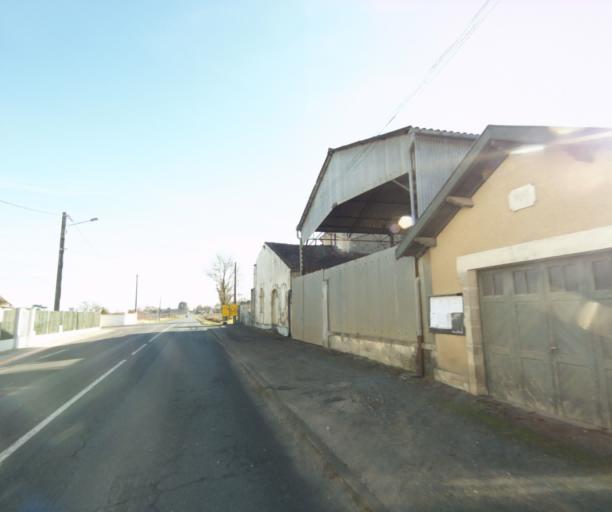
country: FR
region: Poitou-Charentes
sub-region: Departement de la Charente-Maritime
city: Burie
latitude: 45.7840
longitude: -0.4312
